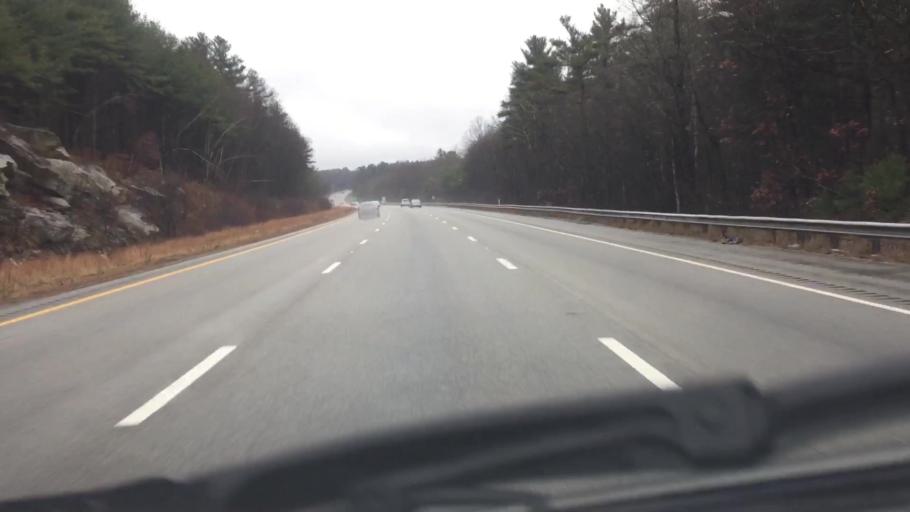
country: US
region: Massachusetts
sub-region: Middlesex County
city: Hopkinton
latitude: 42.2218
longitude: -71.5474
